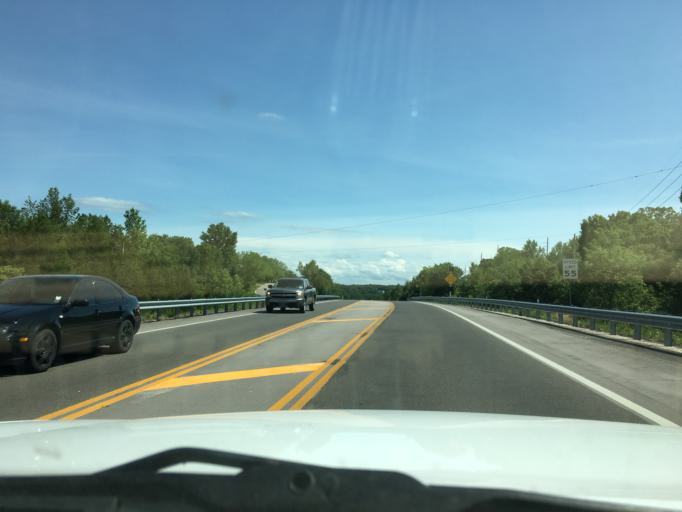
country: US
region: Missouri
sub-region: Franklin County
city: Washington
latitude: 38.5071
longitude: -91.0058
